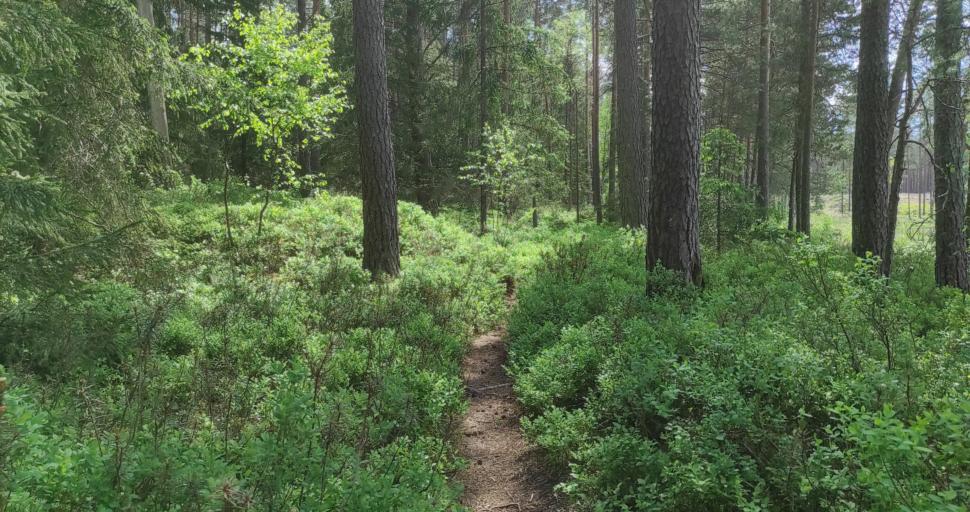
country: LV
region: Talsu Rajons
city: Stende
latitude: 57.1251
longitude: 22.3449
